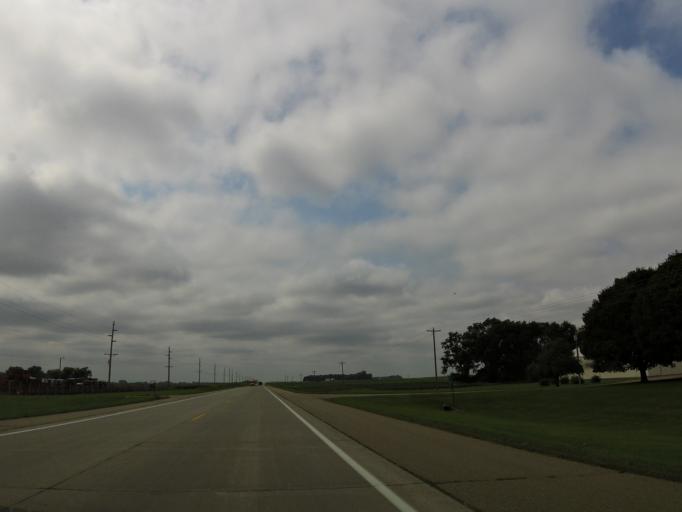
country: US
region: Minnesota
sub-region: Lac qui Parle County
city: Dawson
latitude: 44.9358
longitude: -96.0767
